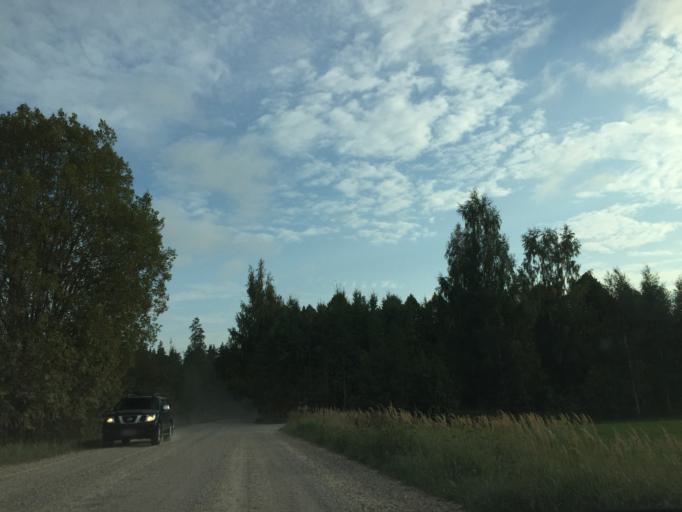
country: LV
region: Ikskile
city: Ikskile
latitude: 56.8123
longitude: 24.4474
